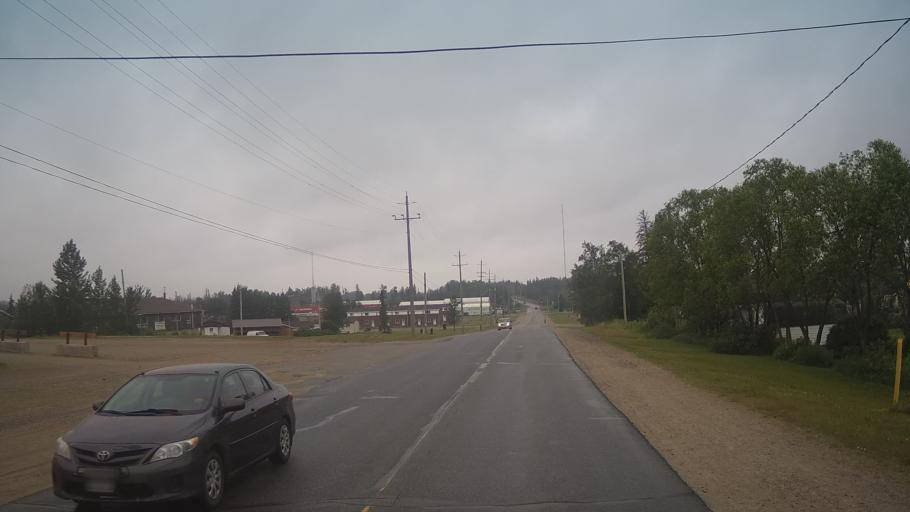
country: CA
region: Ontario
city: Greenstone
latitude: 49.7770
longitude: -86.5335
